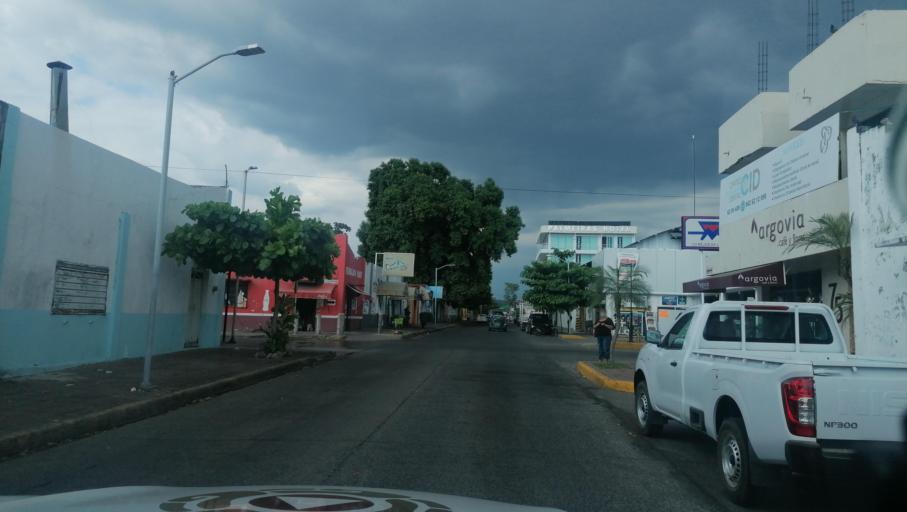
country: MX
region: Chiapas
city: Tapachula
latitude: 14.9091
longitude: -92.2557
